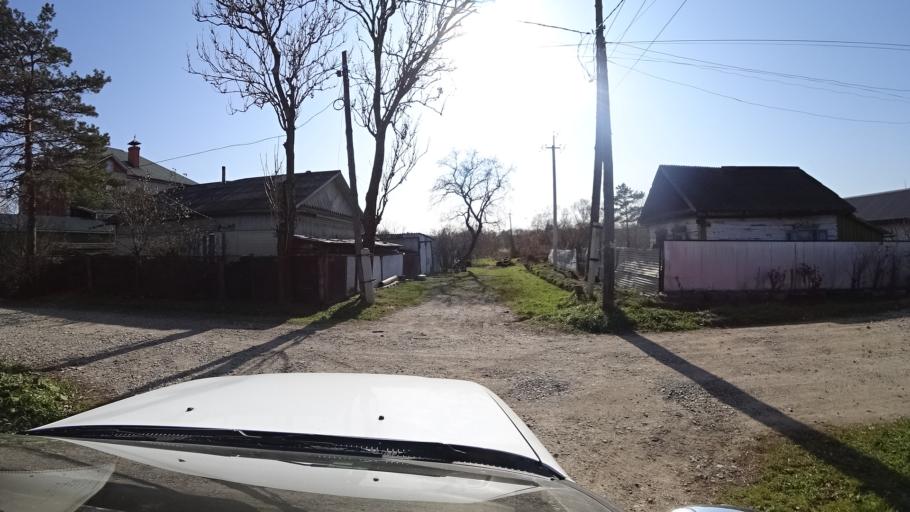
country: RU
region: Primorskiy
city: Dal'nerechensk
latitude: 45.9244
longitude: 133.7181
